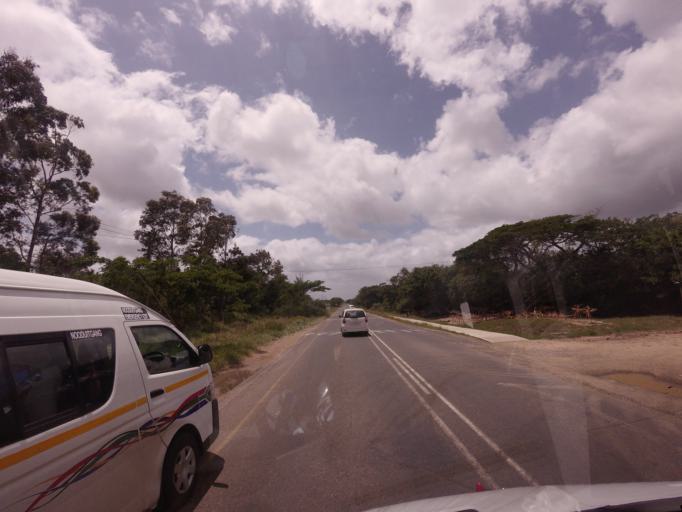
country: ZA
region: KwaZulu-Natal
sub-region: uMkhanyakude District Municipality
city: Mtubatuba
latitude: -28.3758
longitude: 32.3779
